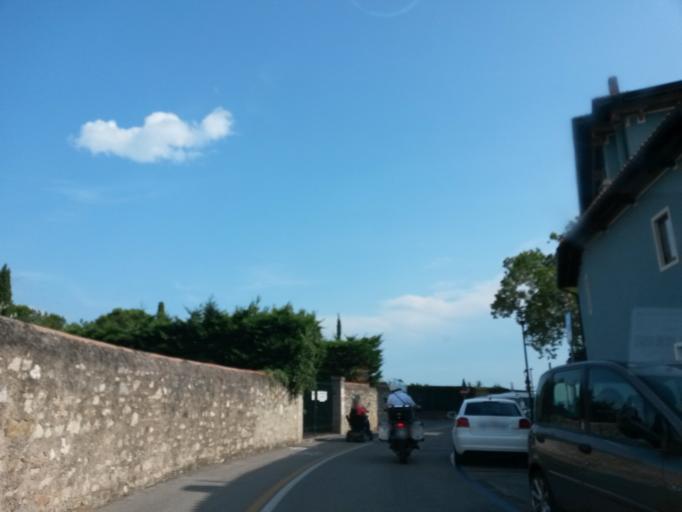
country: IT
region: Lombardy
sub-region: Provincia di Brescia
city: Toscolano Maderno
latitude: 45.6317
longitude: 10.6123
